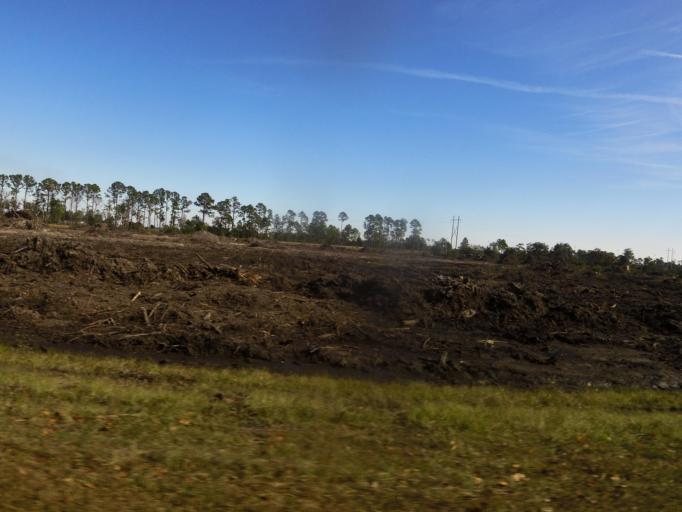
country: US
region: Georgia
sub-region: Glynn County
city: Brunswick
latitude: 31.1319
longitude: -81.5552
